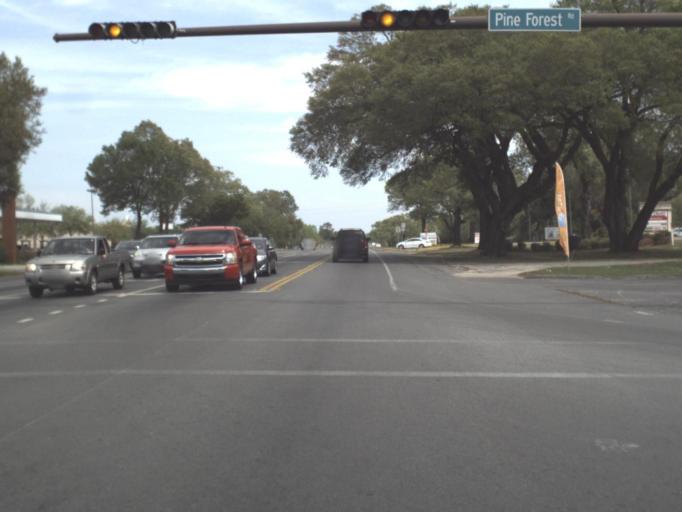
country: US
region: Florida
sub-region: Escambia County
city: Ensley
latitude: 30.5342
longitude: -87.3131
